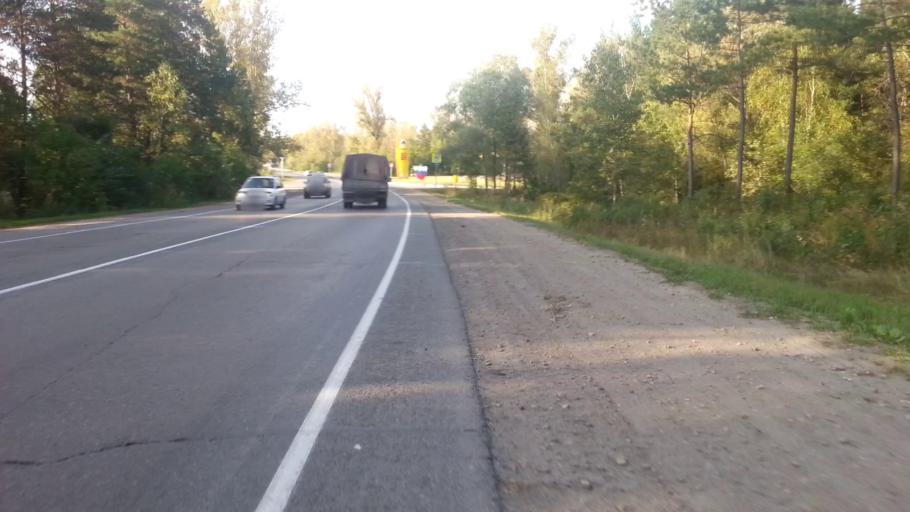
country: RU
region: Altai Krai
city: Yuzhnyy
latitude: 53.3025
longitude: 83.7039
